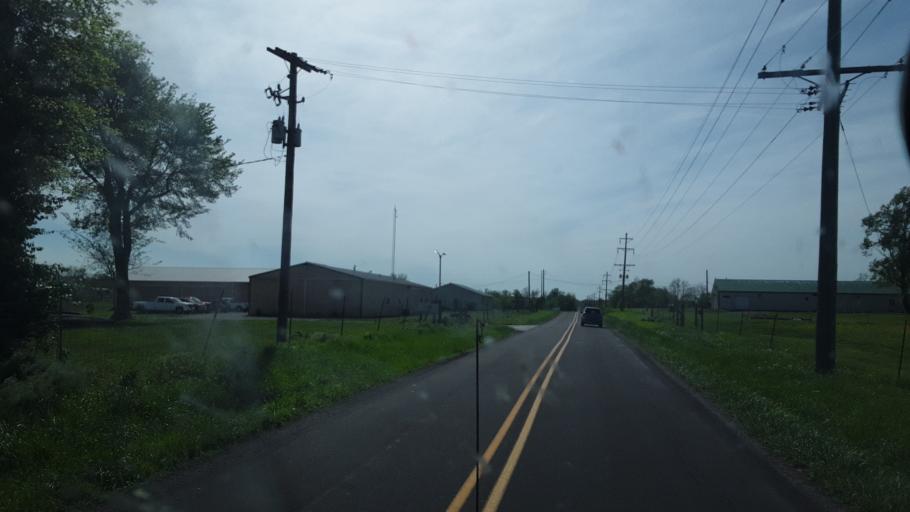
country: US
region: Illinois
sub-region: Jackson County
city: Carbondale
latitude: 37.7010
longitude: -89.2420
